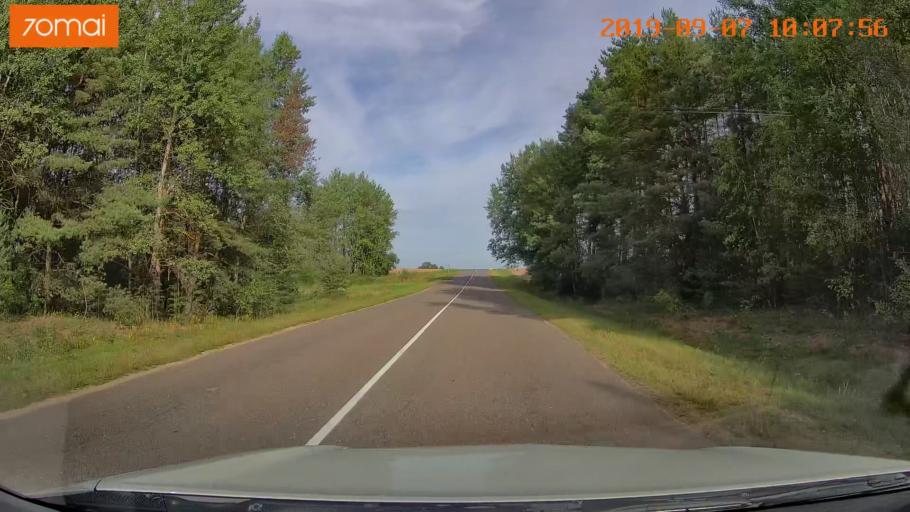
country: BY
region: Grodnenskaya
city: Voranava
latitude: 54.0819
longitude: 25.3938
